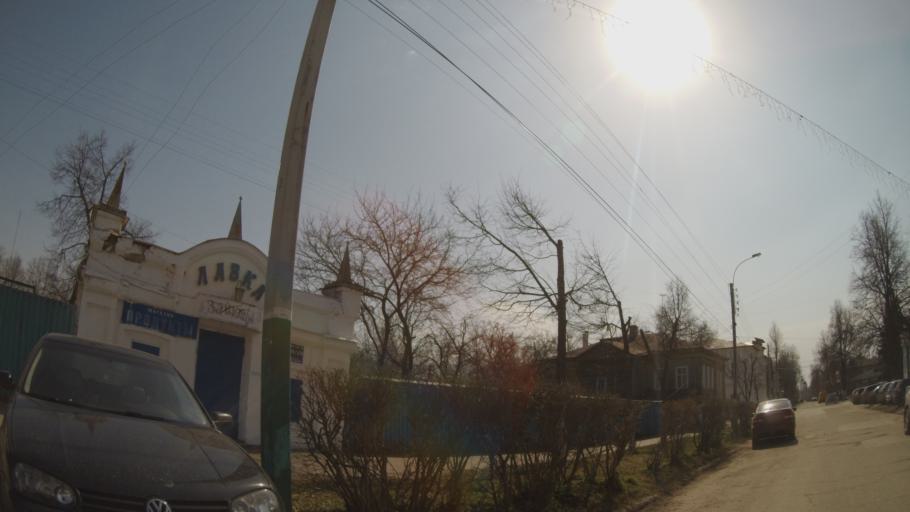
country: RU
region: Nizjnij Novgorod
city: Arzamas
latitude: 55.3903
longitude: 43.8187
